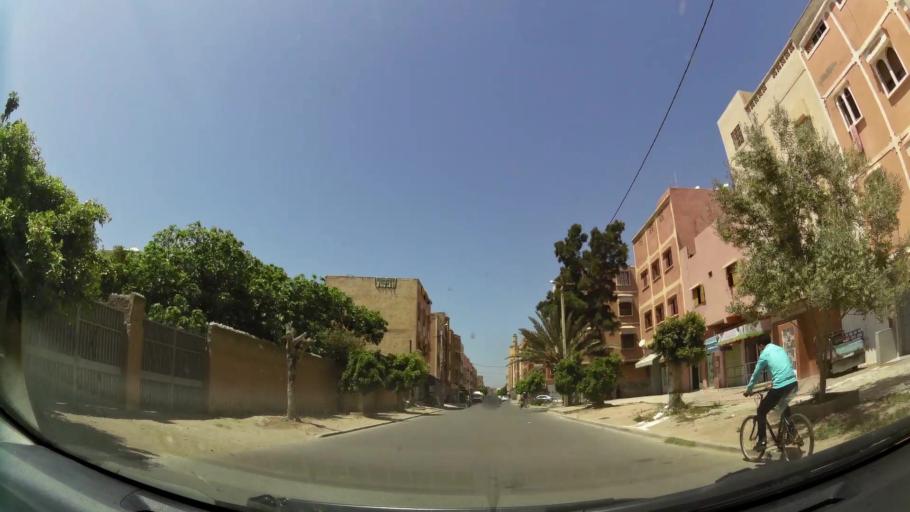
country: MA
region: Souss-Massa-Draa
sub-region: Inezgane-Ait Mellou
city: Inezgane
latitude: 30.3469
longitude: -9.4929
